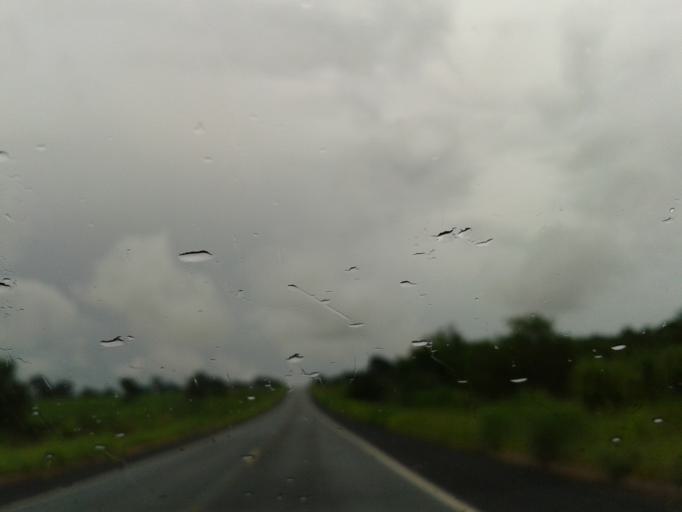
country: BR
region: Minas Gerais
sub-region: Santa Vitoria
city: Santa Vitoria
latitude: -19.1593
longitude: -50.1115
